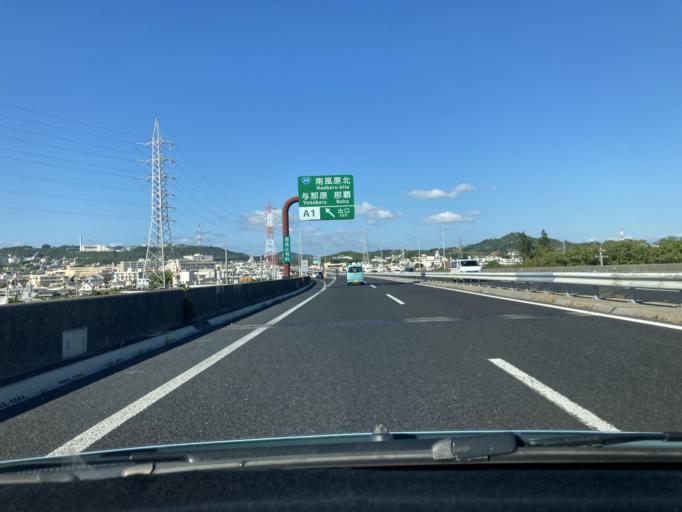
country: JP
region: Okinawa
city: Tomigusuku
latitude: 26.1930
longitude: 127.7393
